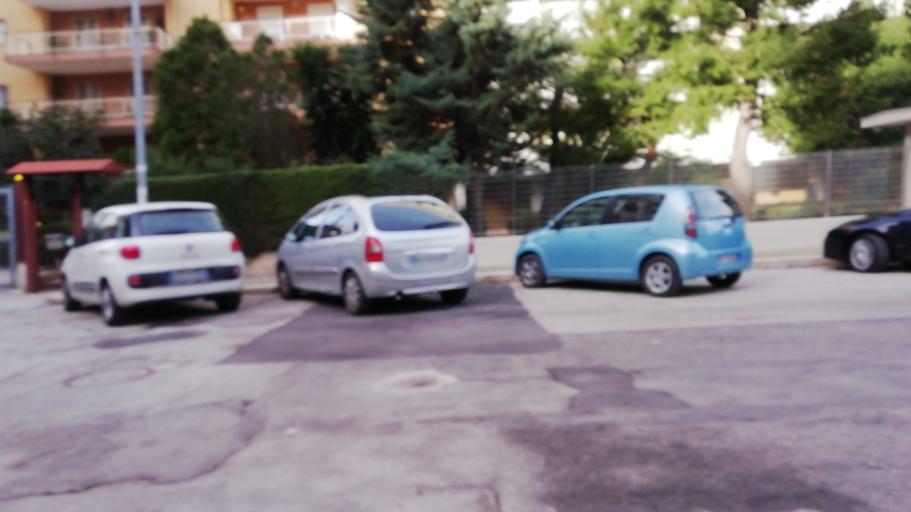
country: IT
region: Apulia
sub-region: Provincia di Bari
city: Triggiano
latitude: 41.1034
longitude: 16.9182
